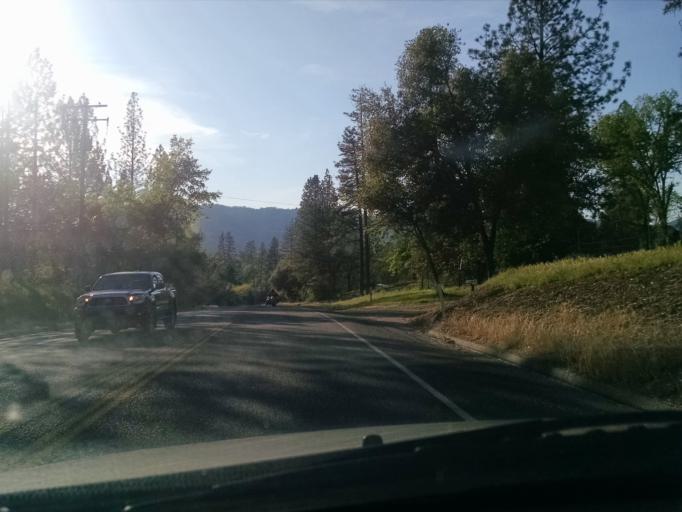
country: US
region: California
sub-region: Madera County
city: Ahwahnee
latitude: 37.3450
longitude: -119.7128
